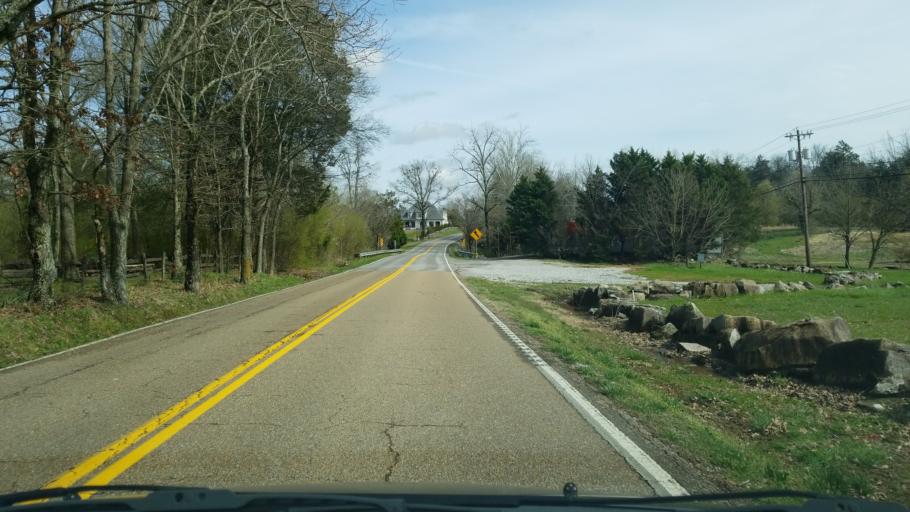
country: US
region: Tennessee
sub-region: Hamilton County
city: Harrison
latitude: 35.1398
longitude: -85.0665
